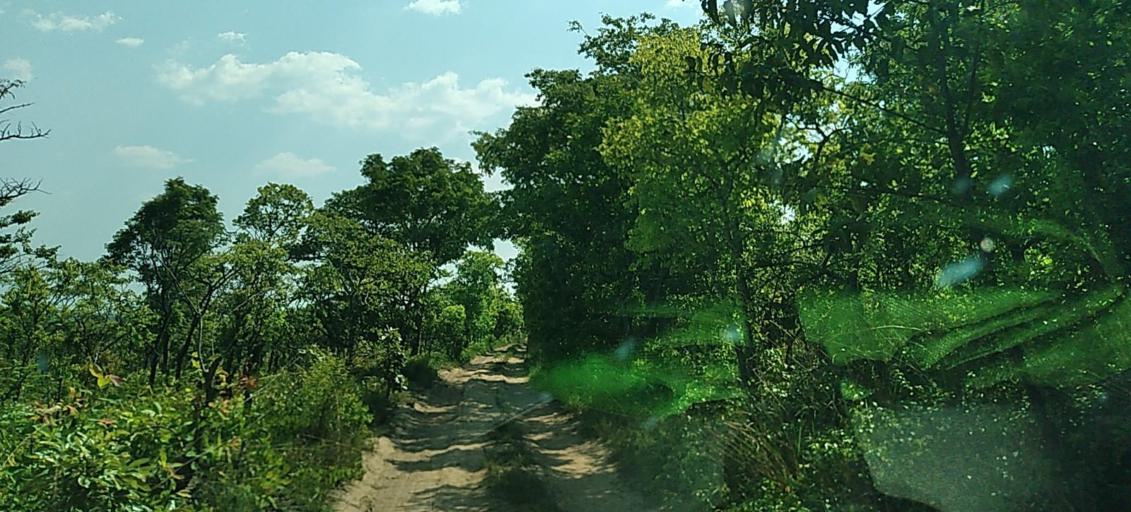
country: CD
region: Katanga
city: Kolwezi
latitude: -11.2665
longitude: 24.9992
